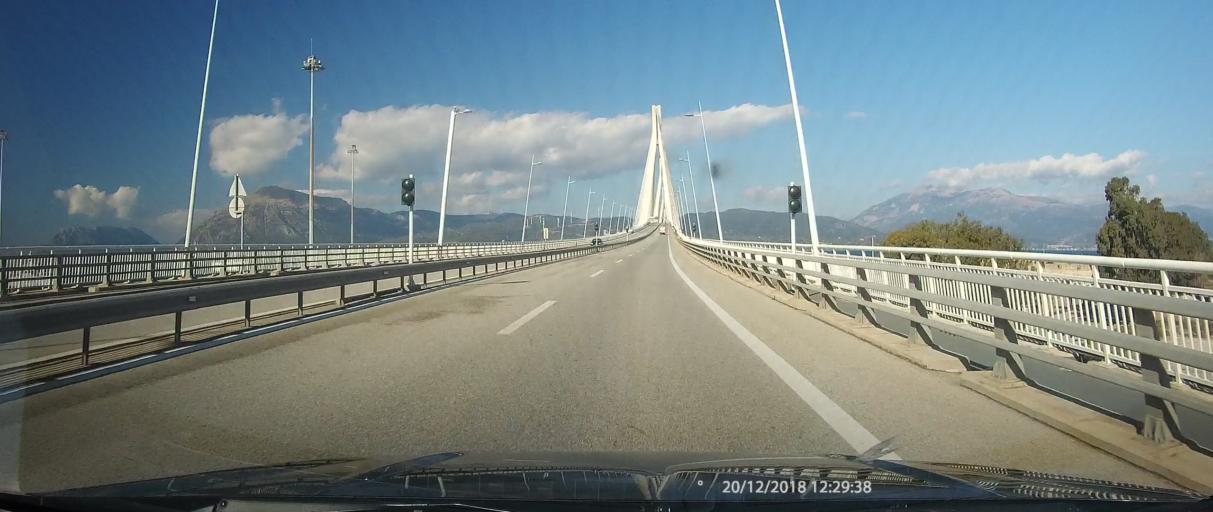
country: GR
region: West Greece
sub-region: Nomos Achaias
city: Rio
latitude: 38.3087
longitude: 21.7807
